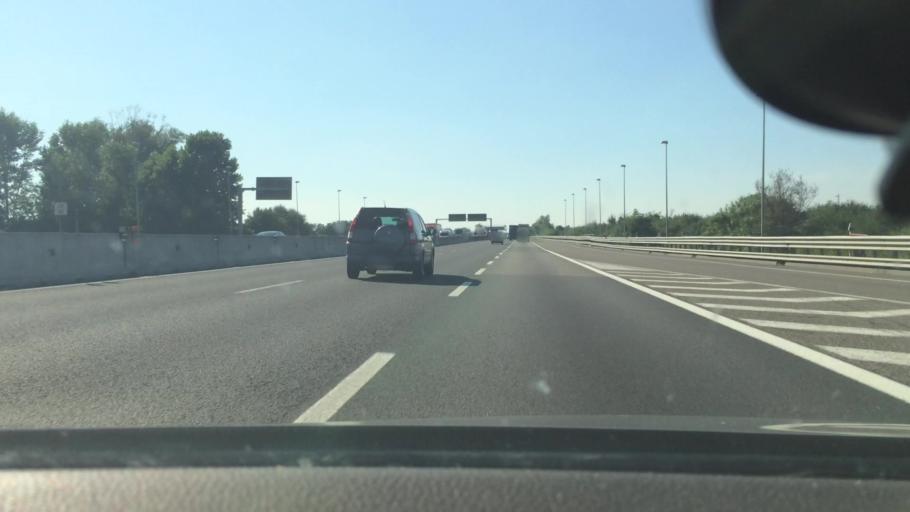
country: IT
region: Lombardy
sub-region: Provincia di Lodi
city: Borgo San Giovanni
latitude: 45.2808
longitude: 9.4406
